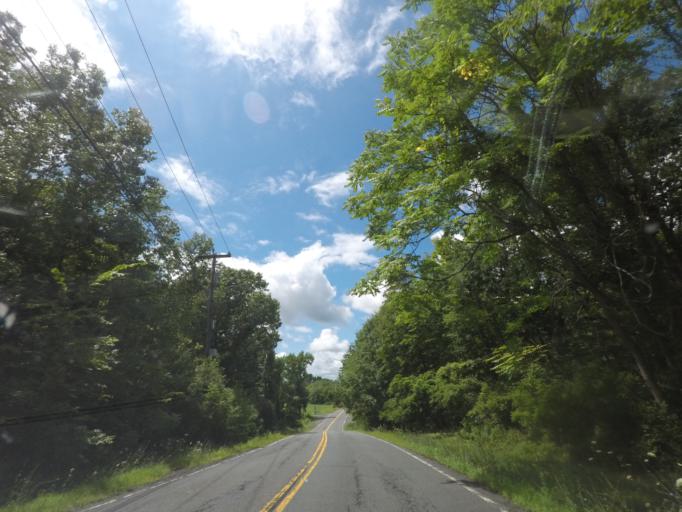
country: US
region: New York
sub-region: Rensselaer County
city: Wynantskill
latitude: 42.6685
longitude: -73.6484
